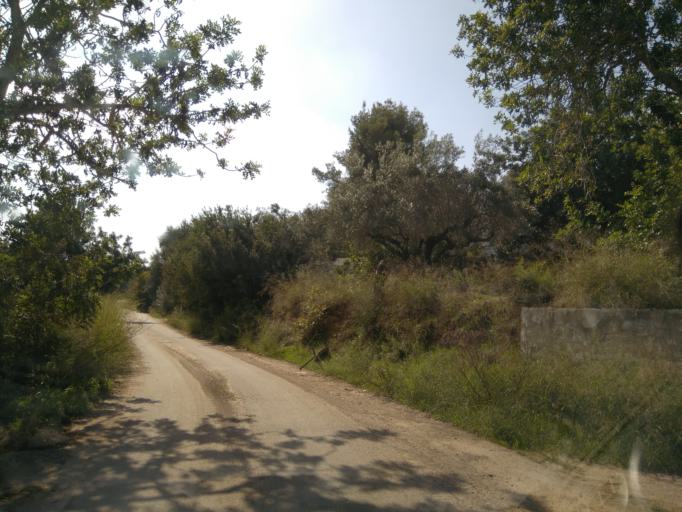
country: ES
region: Valencia
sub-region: Provincia de Valencia
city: Tous
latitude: 39.1799
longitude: -0.6016
